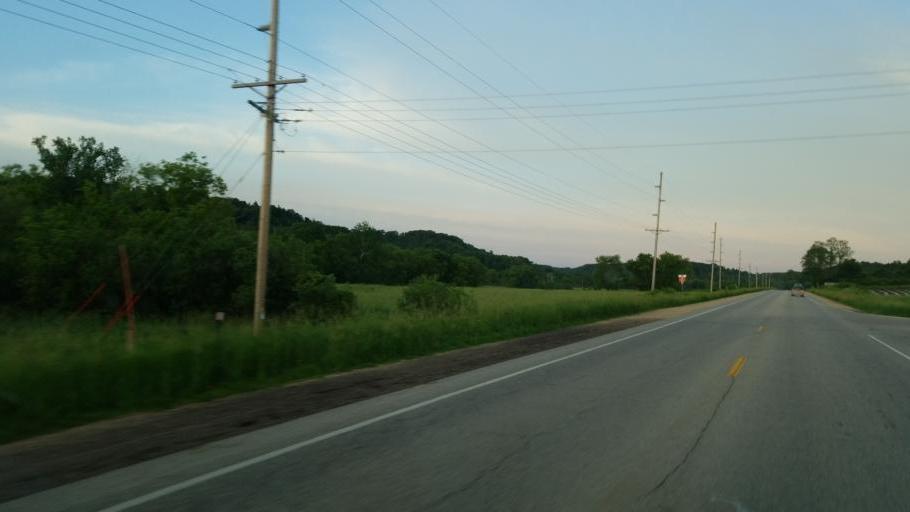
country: US
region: Wisconsin
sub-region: Monroe County
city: Tomah
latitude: 43.8286
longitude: -90.4613
